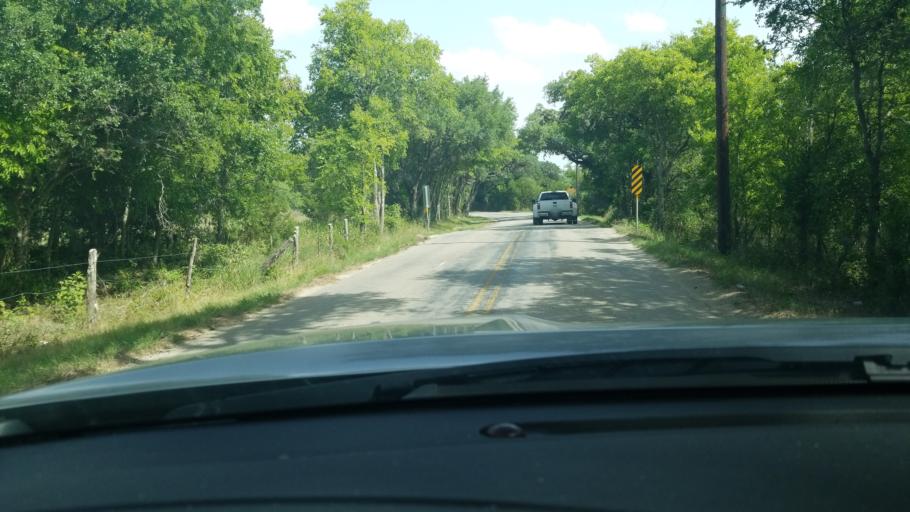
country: US
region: Texas
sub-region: Comal County
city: Bulverde
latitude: 29.7461
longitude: -98.4565
